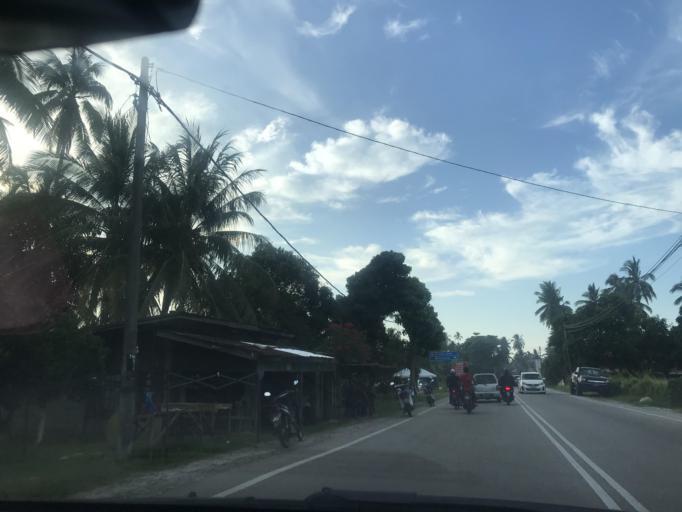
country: MY
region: Kelantan
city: Peringat
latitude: 6.1239
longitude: 102.3568
